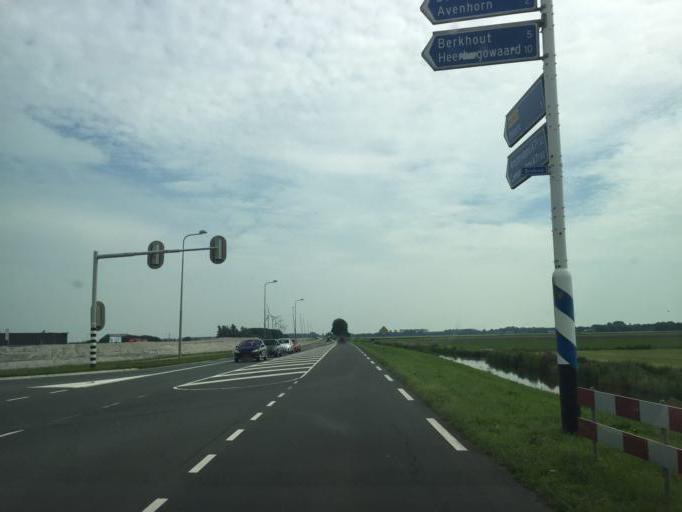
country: NL
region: North Holland
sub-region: Gemeente Opmeer
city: Opmeer
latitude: 52.6213
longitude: 4.9673
